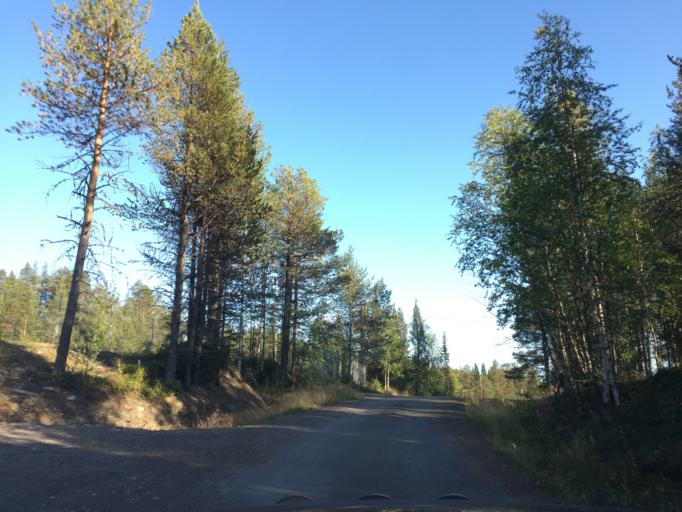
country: SE
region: Norrbotten
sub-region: Gallivare Kommun
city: Malmberget
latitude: 67.6544
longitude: 21.0373
